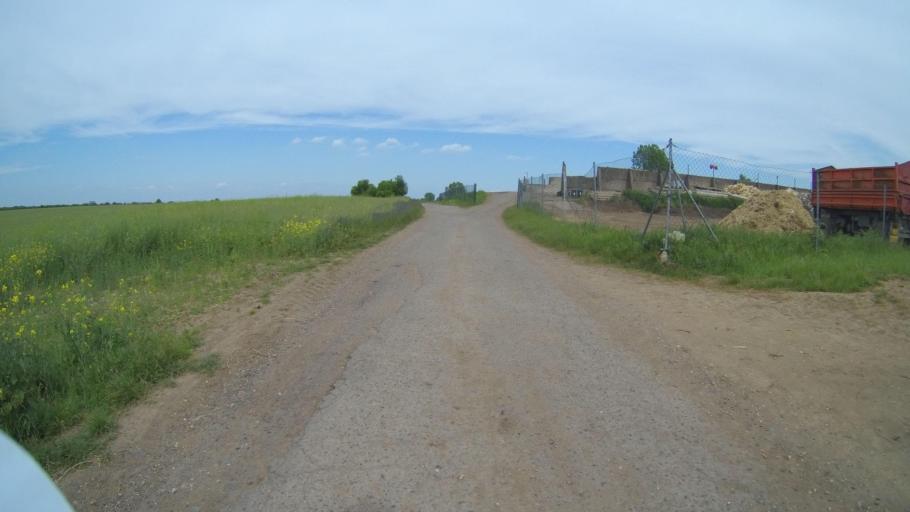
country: CZ
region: Central Bohemia
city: Zdiby
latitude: 50.1647
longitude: 14.4628
